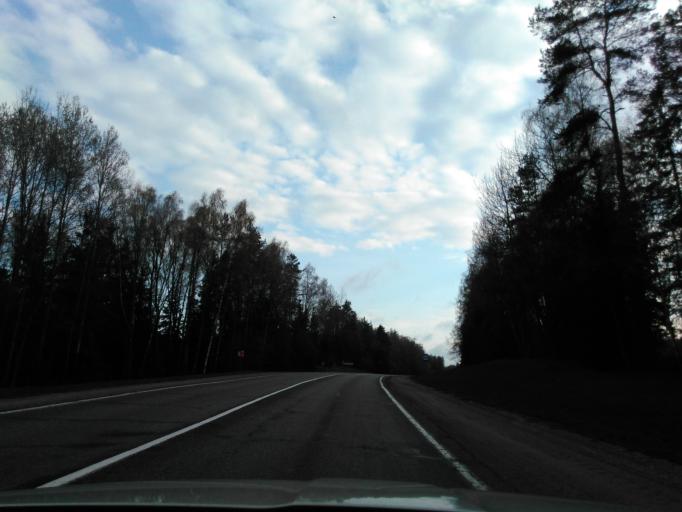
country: BY
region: Minsk
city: Lahoysk
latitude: 54.2877
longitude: 27.8702
